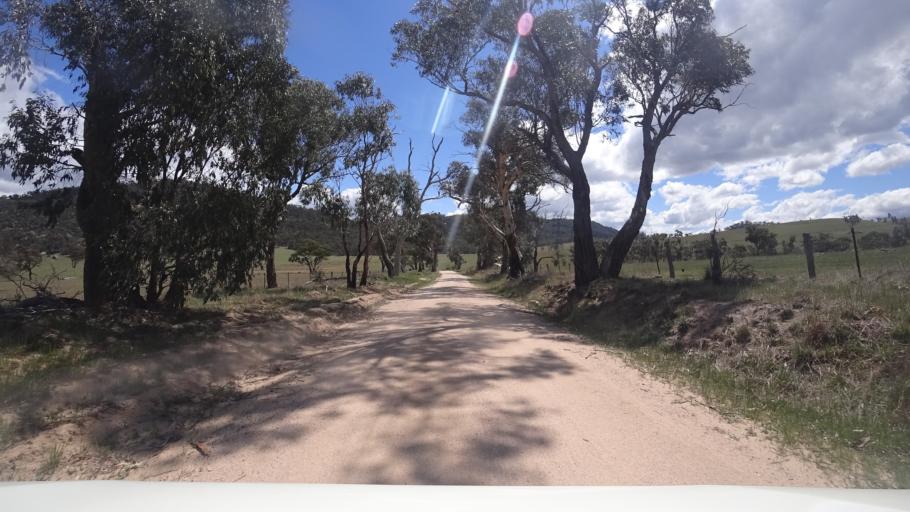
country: AU
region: New South Wales
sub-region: Oberon
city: Oberon
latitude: -33.5601
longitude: 149.9353
